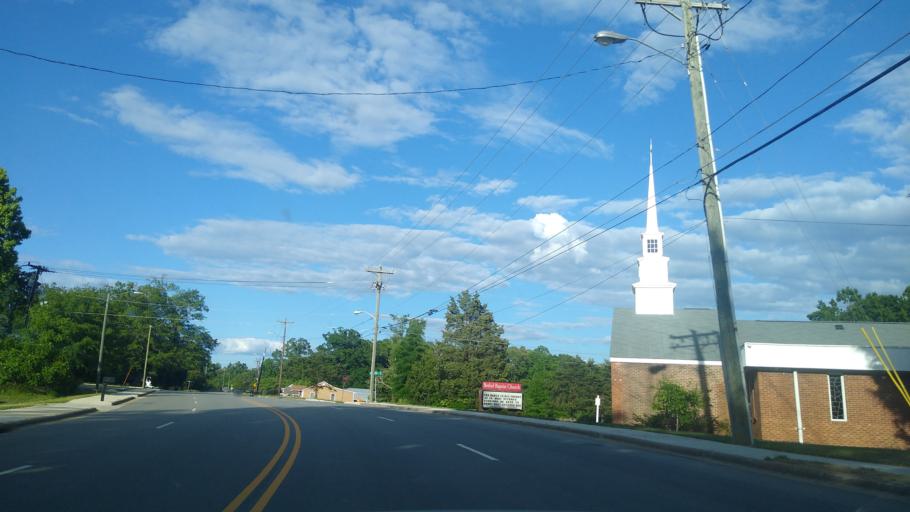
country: US
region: North Carolina
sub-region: Guilford County
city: Greensboro
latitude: 36.1443
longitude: -79.7608
